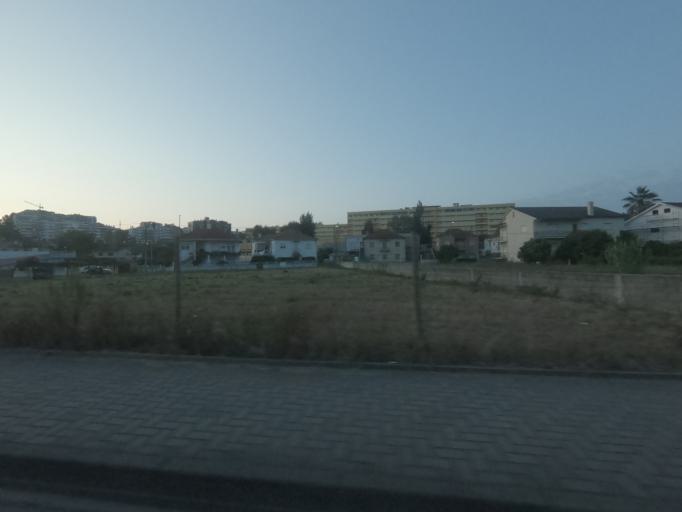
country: PT
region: Leiria
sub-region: Leiria
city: Leiria
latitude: 39.7412
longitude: -8.7944
